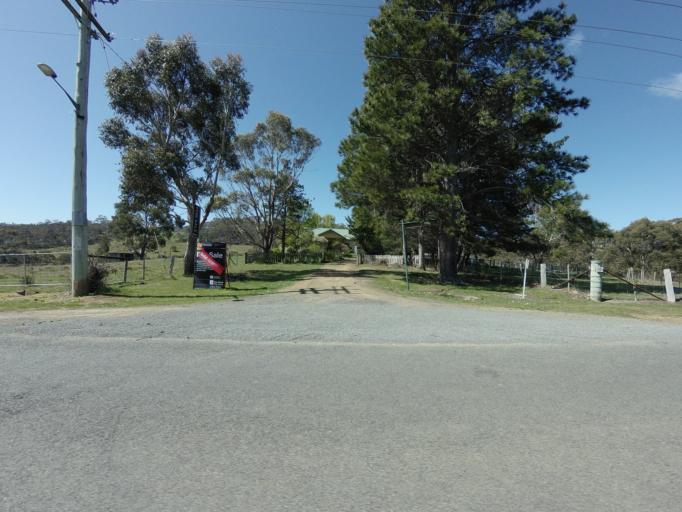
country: AU
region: Tasmania
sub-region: Derwent Valley
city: New Norfolk
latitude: -42.6222
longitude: 146.7208
